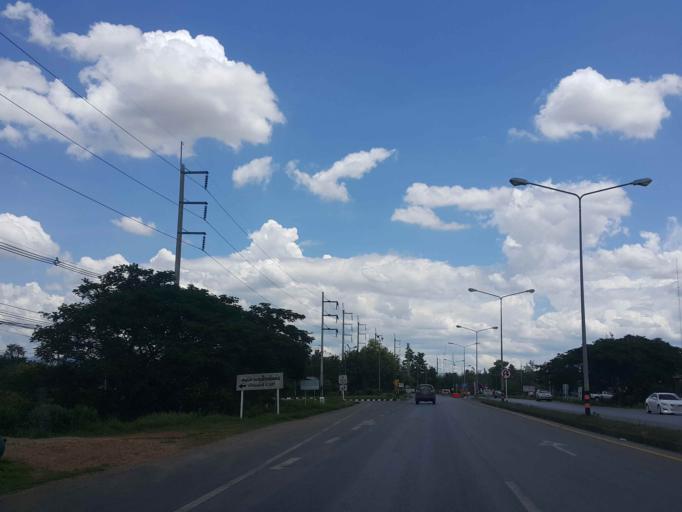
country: TH
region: Phrae
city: Nong Muang Khai
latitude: 18.2118
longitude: 100.1991
